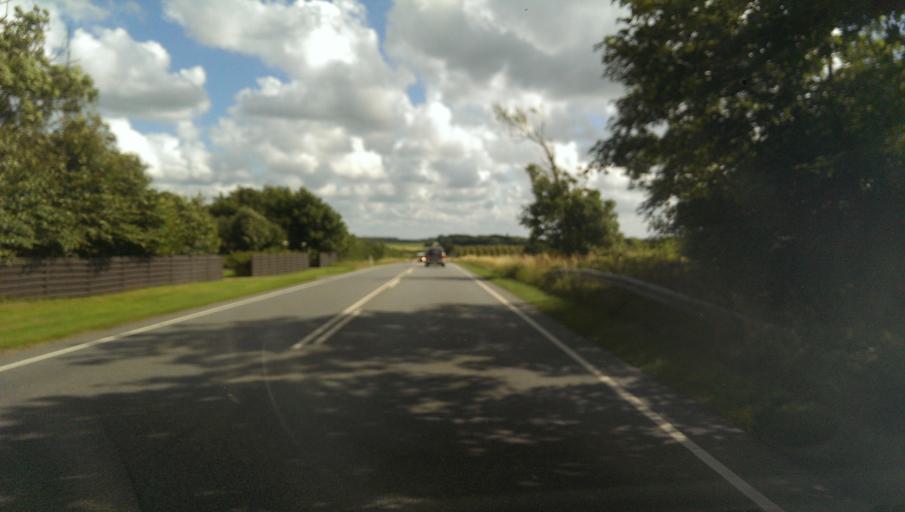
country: DK
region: South Denmark
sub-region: Varde Kommune
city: Varde
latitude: 55.6839
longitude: 8.4922
